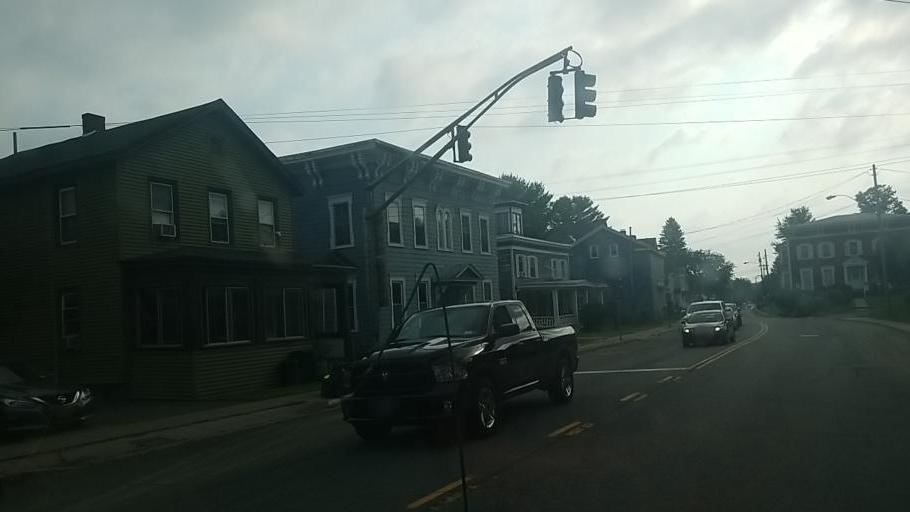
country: US
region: New York
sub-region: Fulton County
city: Johnstown
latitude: 43.0065
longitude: -74.3682
